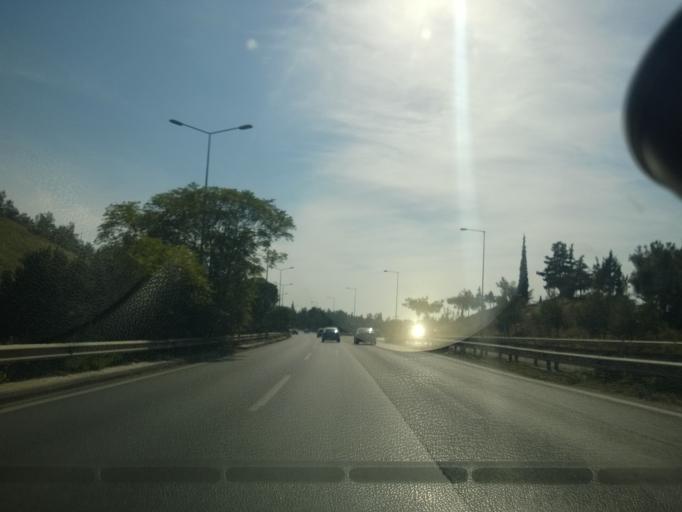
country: GR
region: Central Macedonia
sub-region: Nomos Thessalonikis
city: Agios Pavlos
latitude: 40.6539
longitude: 22.9662
